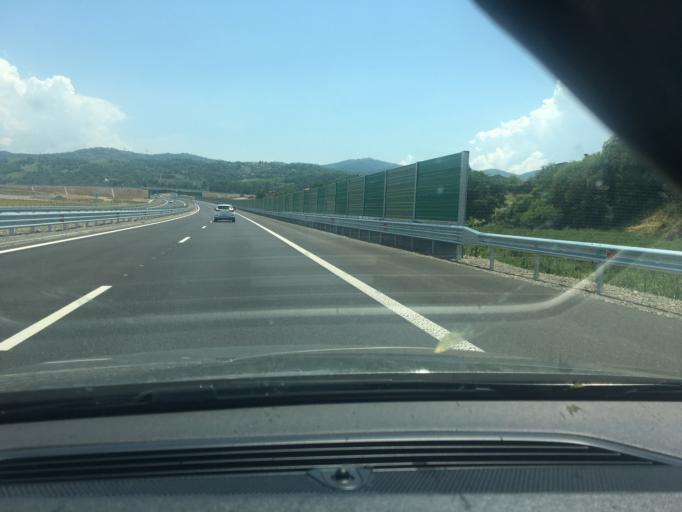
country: BG
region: Blagoevgrad
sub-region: Obshtina Blagoevgrad
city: Blagoevgrad
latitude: 41.9899
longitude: 23.0548
